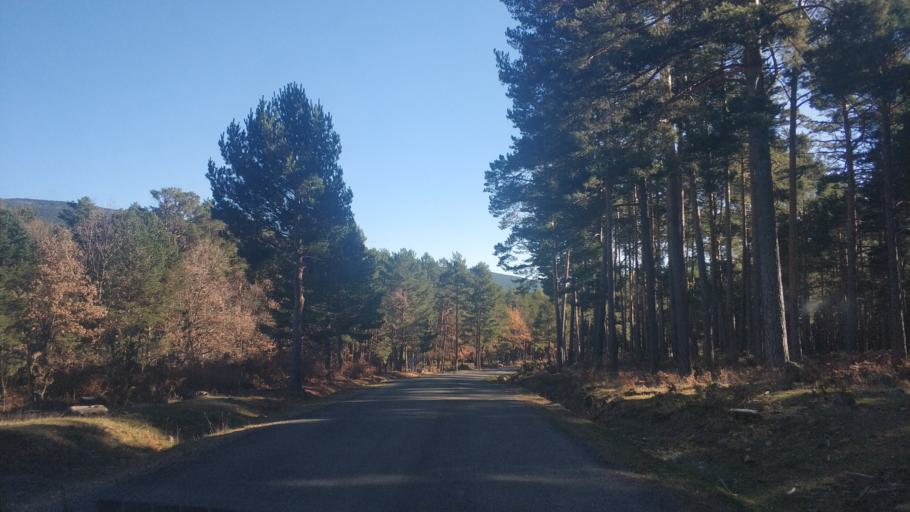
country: ES
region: Castille and Leon
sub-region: Provincia de Soria
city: Vinuesa
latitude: 41.9622
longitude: -2.7877
